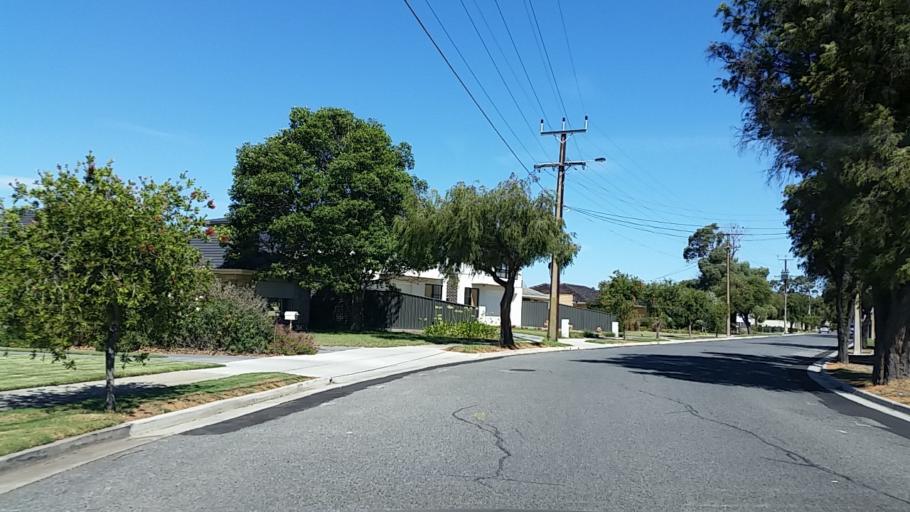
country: AU
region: South Australia
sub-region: Charles Sturt
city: Henley Beach
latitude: -34.9239
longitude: 138.5103
